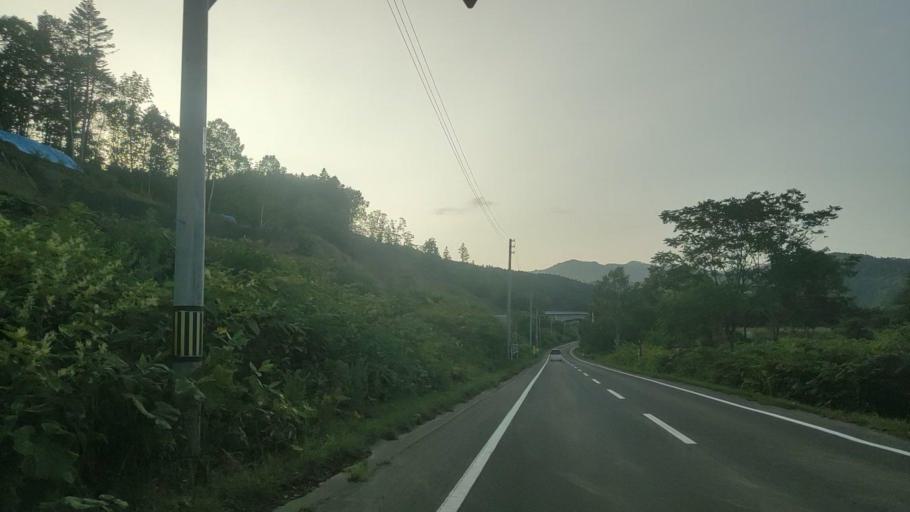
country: JP
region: Hokkaido
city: Bibai
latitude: 43.2243
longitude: 142.0473
